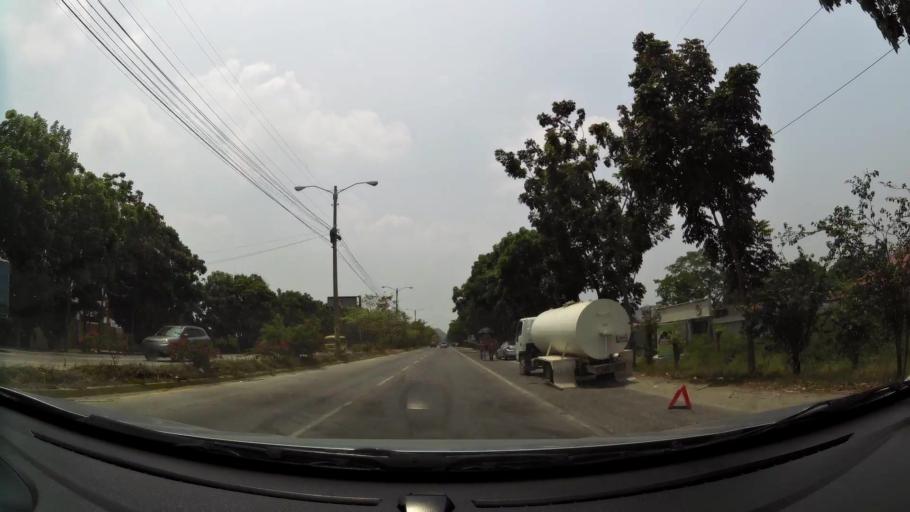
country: HN
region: Cortes
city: Chotepe
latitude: 15.4734
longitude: -87.9704
